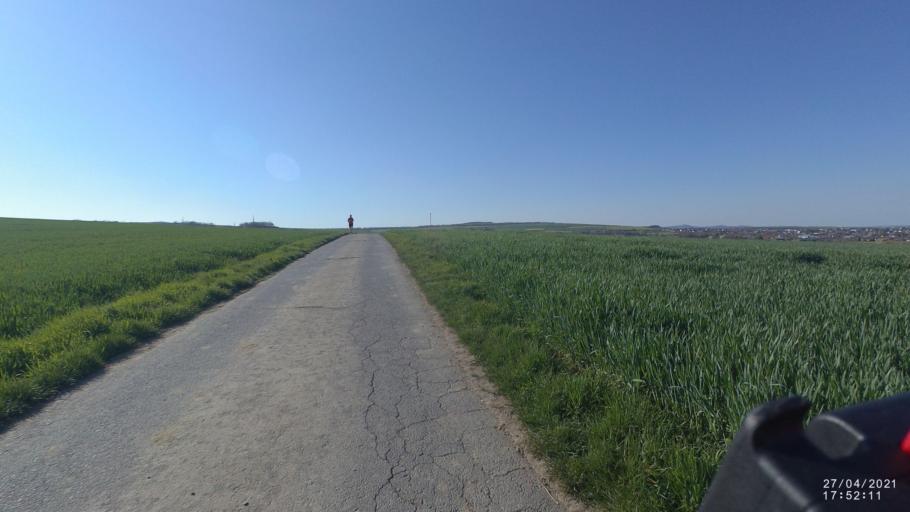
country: DE
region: Rheinland-Pfalz
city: Mertloch
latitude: 50.2827
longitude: 7.3028
